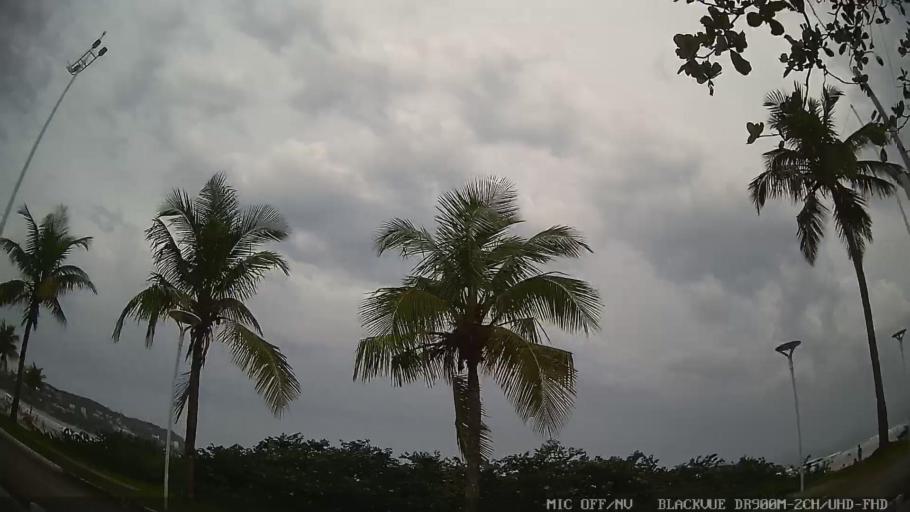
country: BR
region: Sao Paulo
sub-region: Guaruja
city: Guaruja
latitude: -23.9853
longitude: -46.2105
